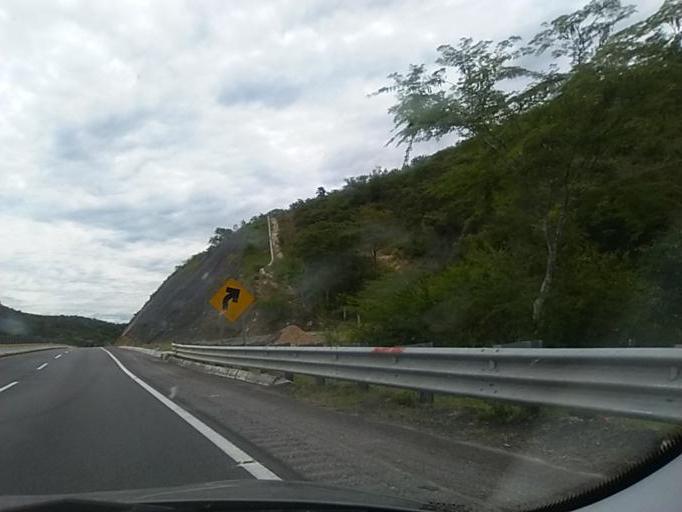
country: MX
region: Guerrero
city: Copalillo
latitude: 18.1408
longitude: -99.2098
